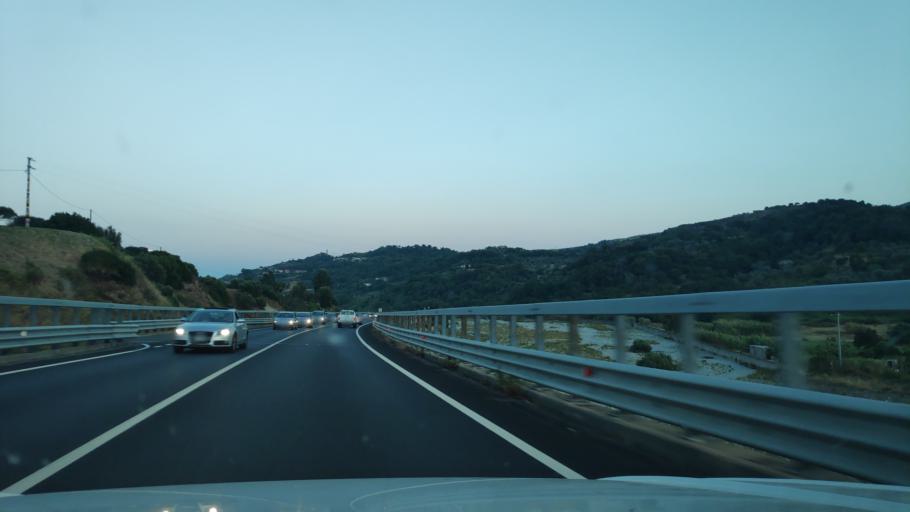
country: IT
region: Calabria
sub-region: Provincia di Reggio Calabria
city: Grotteria
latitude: 38.3489
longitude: 16.2552
